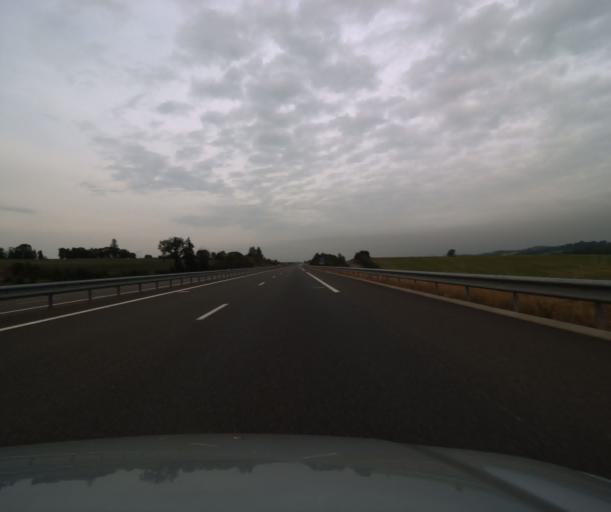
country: FR
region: Midi-Pyrenees
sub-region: Departement du Gers
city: Aubiet
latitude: 43.6536
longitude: 0.7468
